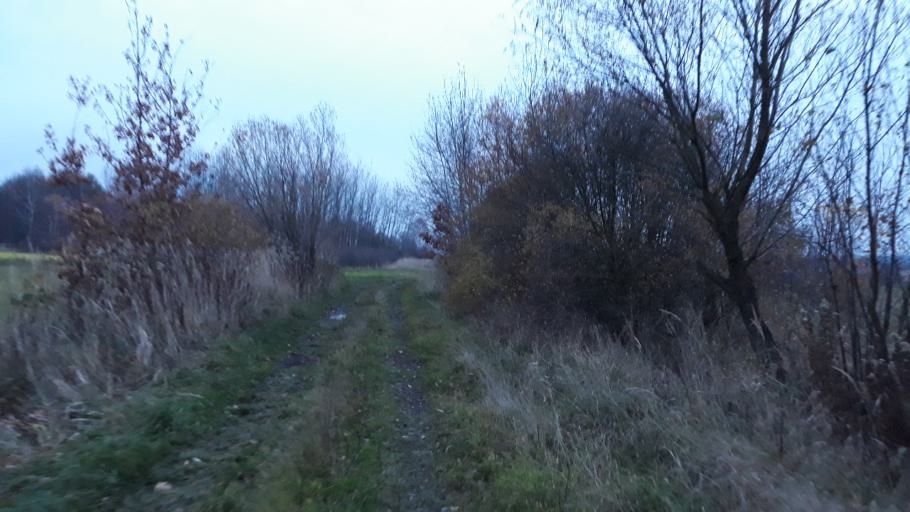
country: PL
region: Lublin Voivodeship
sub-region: Powiat janowski
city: Dzwola
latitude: 50.6644
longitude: 22.5924
